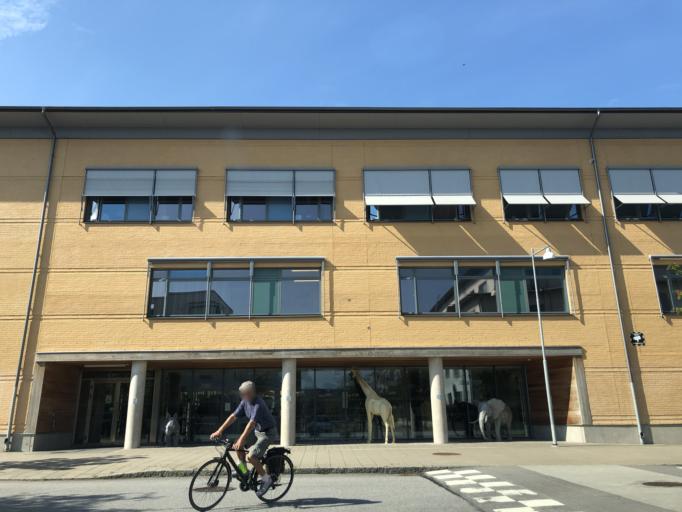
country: SE
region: Vaestra Goetaland
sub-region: Goteborg
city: Majorna
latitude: 57.6990
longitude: 11.9028
